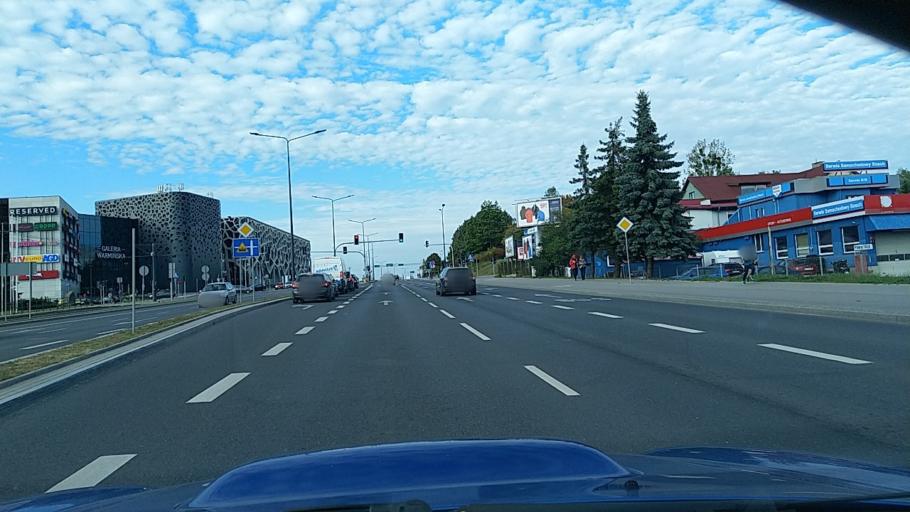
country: PL
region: Warmian-Masurian Voivodeship
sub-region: Powiat olsztynski
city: Olsztyn
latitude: 53.7517
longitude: 20.4864
